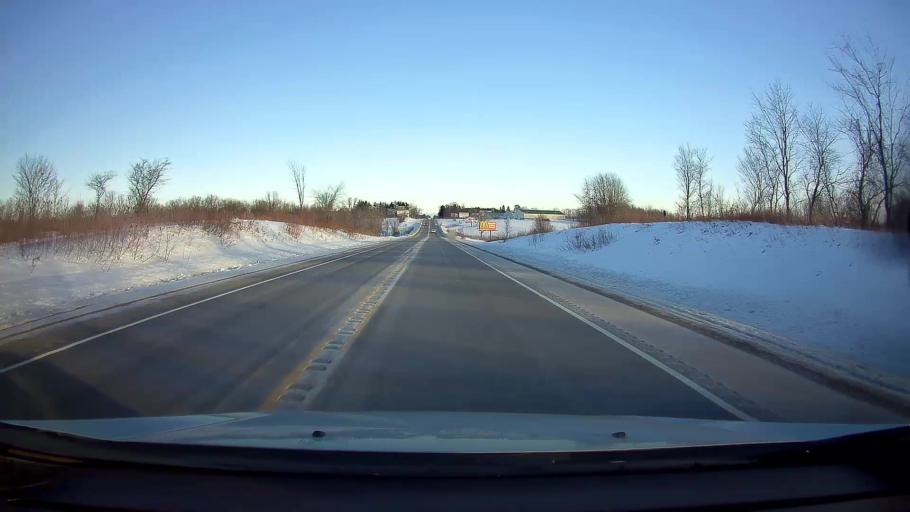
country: US
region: Wisconsin
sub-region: Washburn County
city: Shell Lake
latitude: 45.7656
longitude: -91.9122
